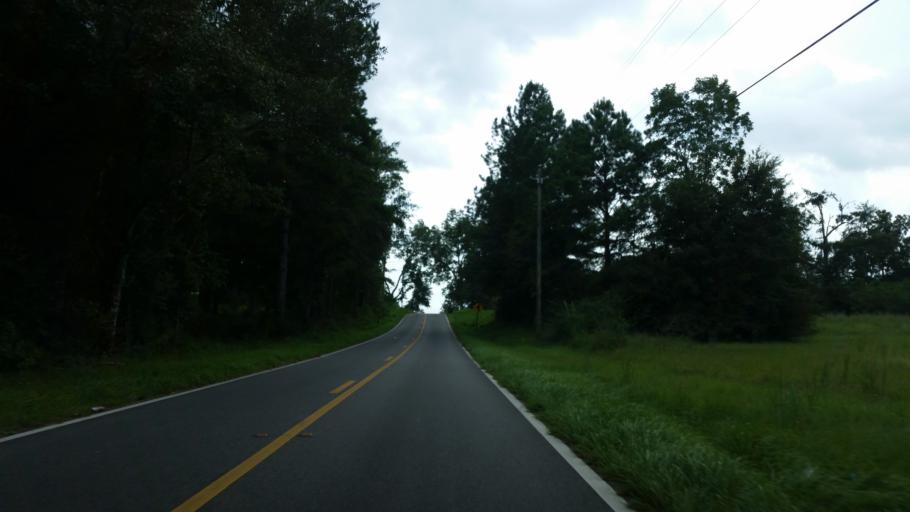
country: US
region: Florida
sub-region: Escambia County
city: Molino
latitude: 30.7007
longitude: -87.4053
